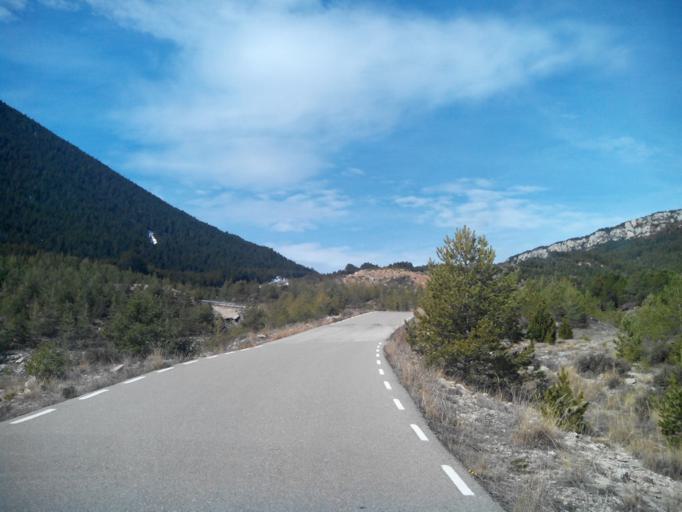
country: ES
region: Catalonia
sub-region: Provincia de Barcelona
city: Vallcebre
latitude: 42.1997
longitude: 1.7951
